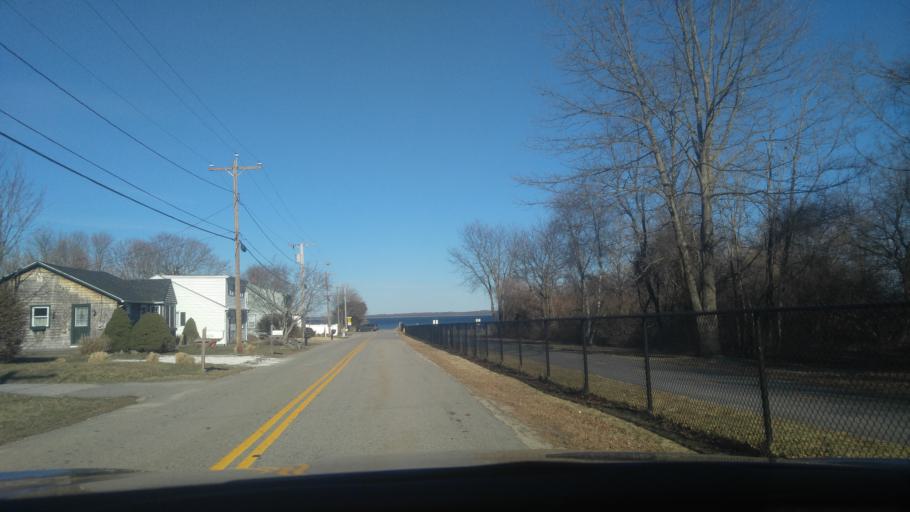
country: US
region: Rhode Island
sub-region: Kent County
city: East Greenwich
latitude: 41.6340
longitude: -71.4095
